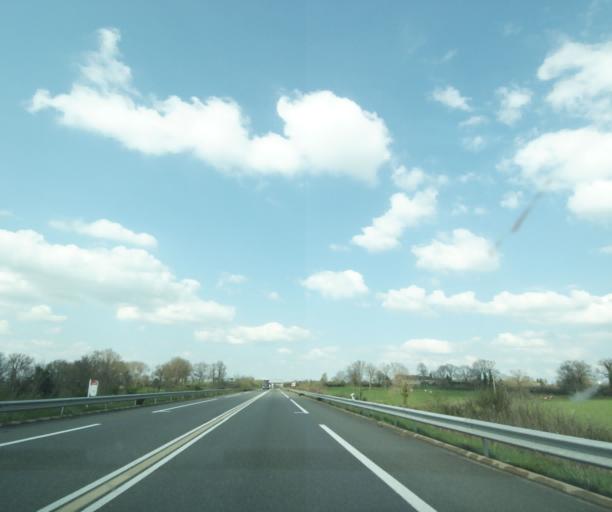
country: FR
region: Auvergne
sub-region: Departement de l'Allier
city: Montmarault
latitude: 46.3872
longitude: 3.0325
